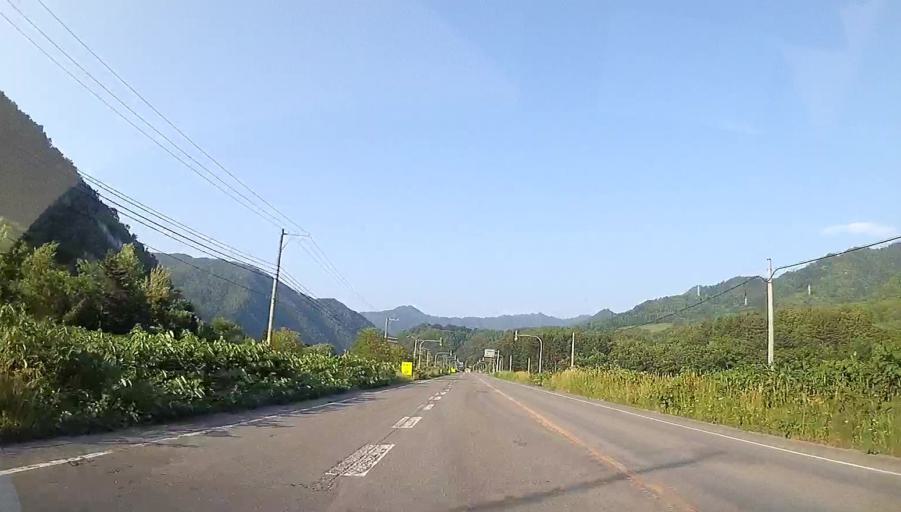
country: JP
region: Hokkaido
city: Shimo-furano
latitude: 42.8957
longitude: 142.5558
